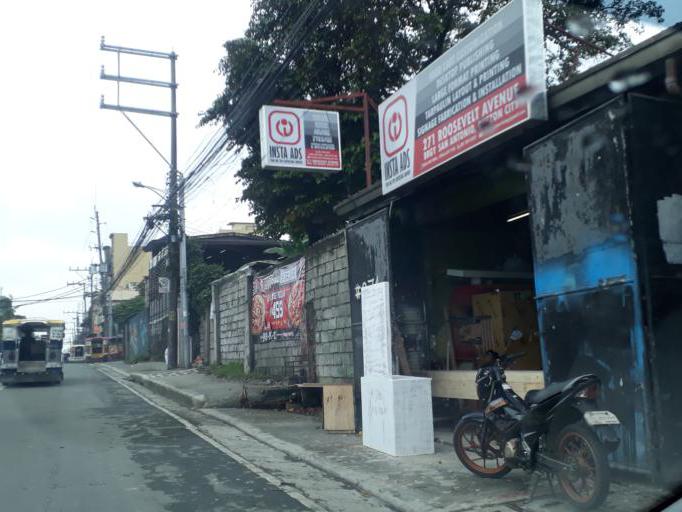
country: PH
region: Calabarzon
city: Del Monte
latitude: 14.6500
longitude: 121.0178
